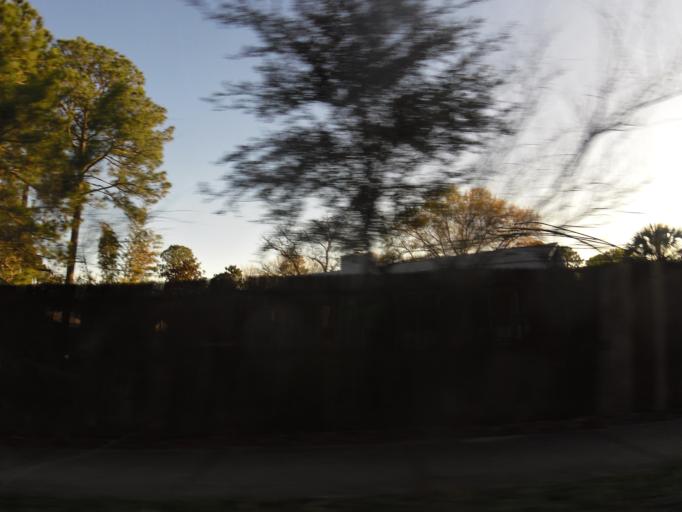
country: US
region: Florida
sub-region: Saint Johns County
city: Fruit Cove
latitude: 30.1722
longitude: -81.5888
